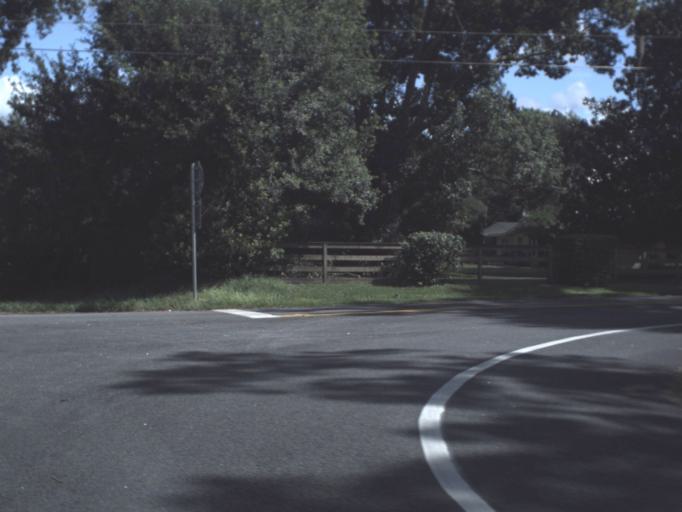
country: US
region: Florida
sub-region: Hillsborough County
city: Plant City
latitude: 28.0383
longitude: -82.1348
